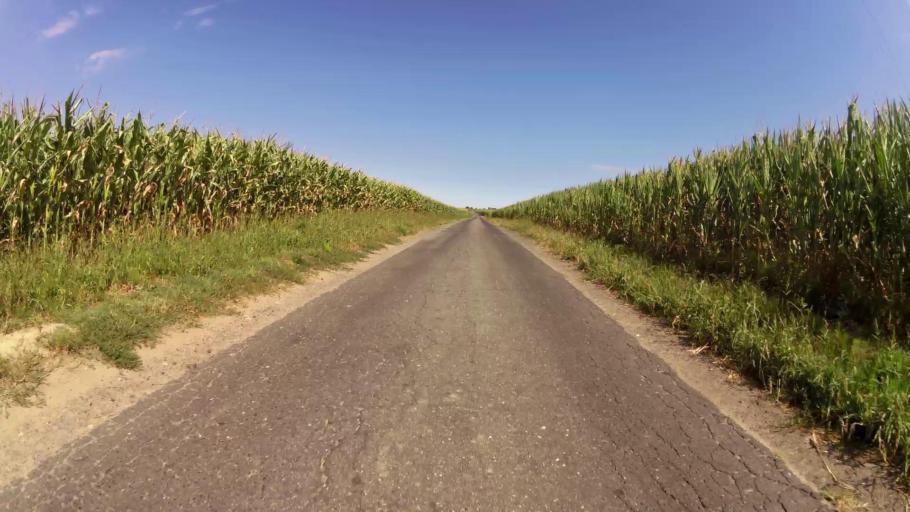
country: PL
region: West Pomeranian Voivodeship
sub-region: Powiat choszczenski
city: Choszczno
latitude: 53.2619
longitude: 15.4355
